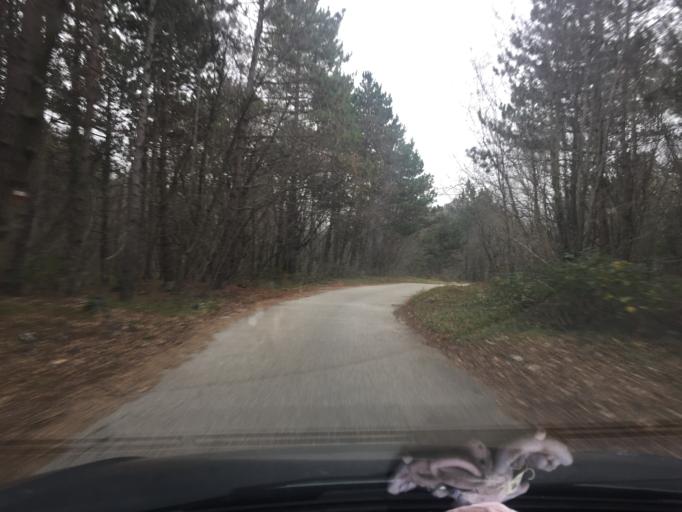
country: IT
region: Friuli Venezia Giulia
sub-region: Provincia di Trieste
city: Zolla
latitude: 45.7235
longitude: 13.7995
